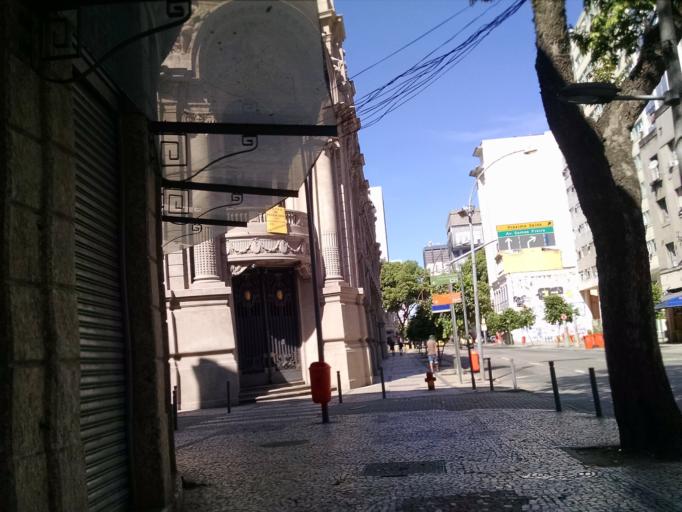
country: BR
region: Rio de Janeiro
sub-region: Rio De Janeiro
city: Rio de Janeiro
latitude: -22.9109
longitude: -43.1854
